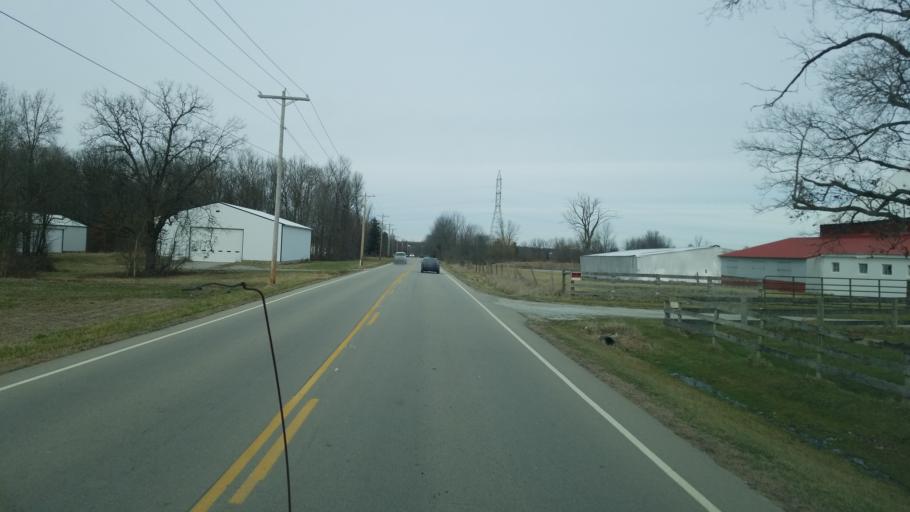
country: US
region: Ohio
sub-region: Adams County
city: Winchester
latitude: 39.0273
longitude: -83.7050
